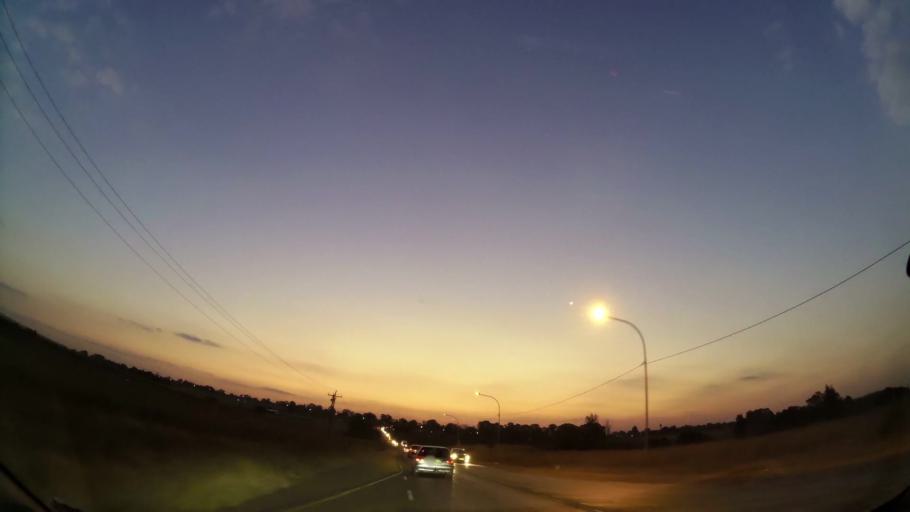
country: ZA
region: Gauteng
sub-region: Ekurhuleni Metropolitan Municipality
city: Benoni
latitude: -26.1019
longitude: 28.3203
